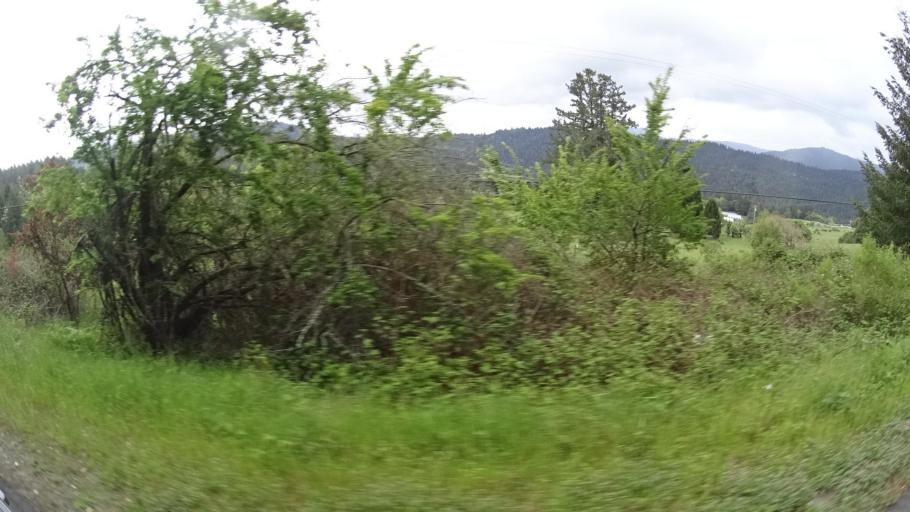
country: US
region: California
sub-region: Humboldt County
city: Redway
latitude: 40.2896
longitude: -123.8087
